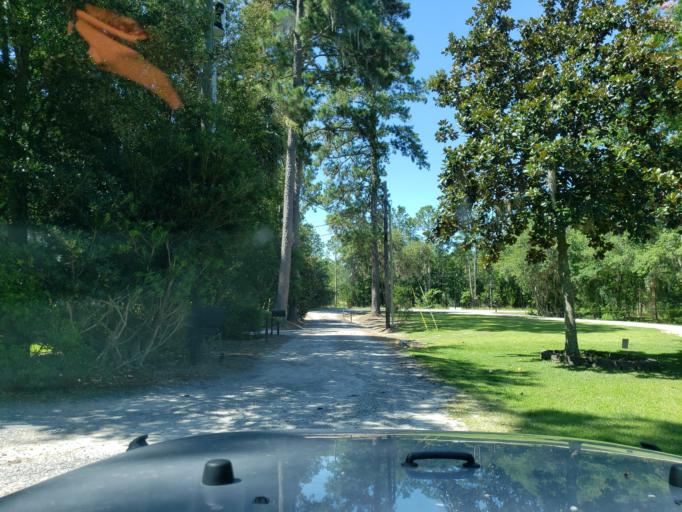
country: US
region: Georgia
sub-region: Chatham County
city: Georgetown
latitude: 31.9631
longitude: -81.2122
